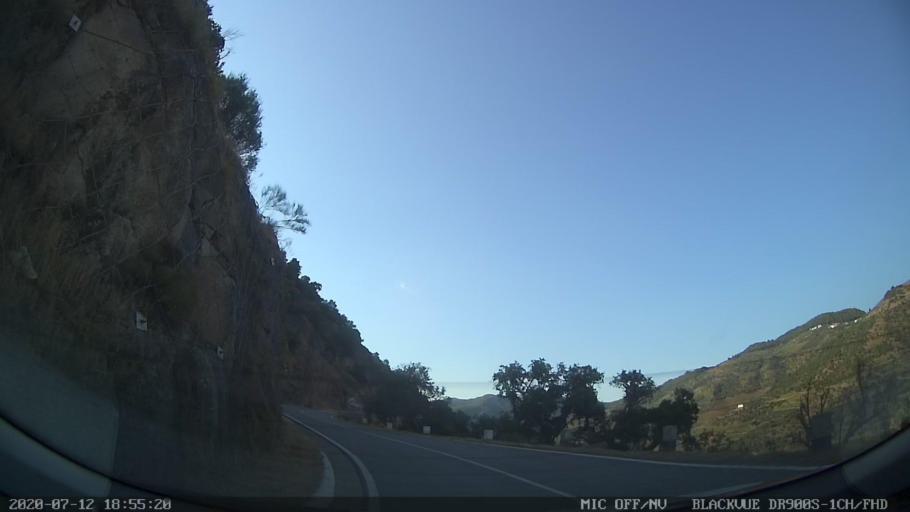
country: PT
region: Viseu
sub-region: Sao Joao da Pesqueira
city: Sao Joao da Pesqueira
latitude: 41.2227
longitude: -7.4234
